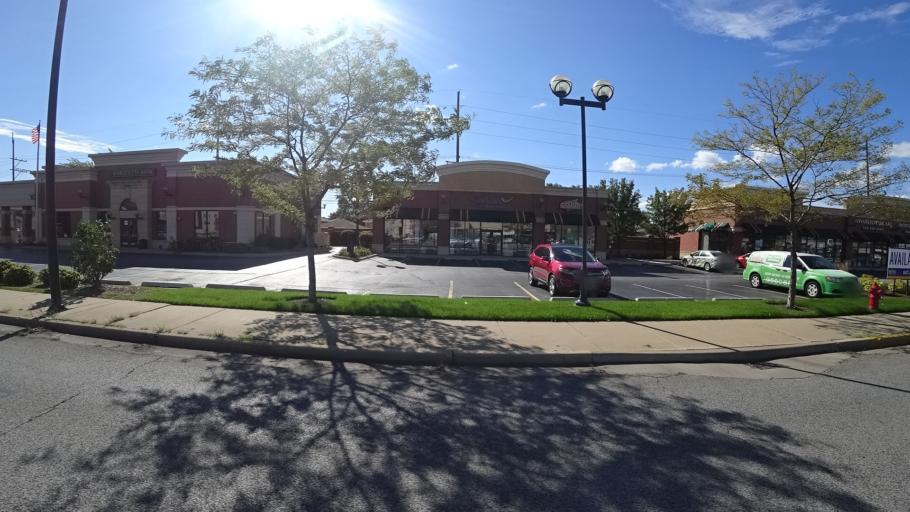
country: US
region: Illinois
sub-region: Cook County
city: Oak Lawn
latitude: 41.7044
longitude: -87.7403
